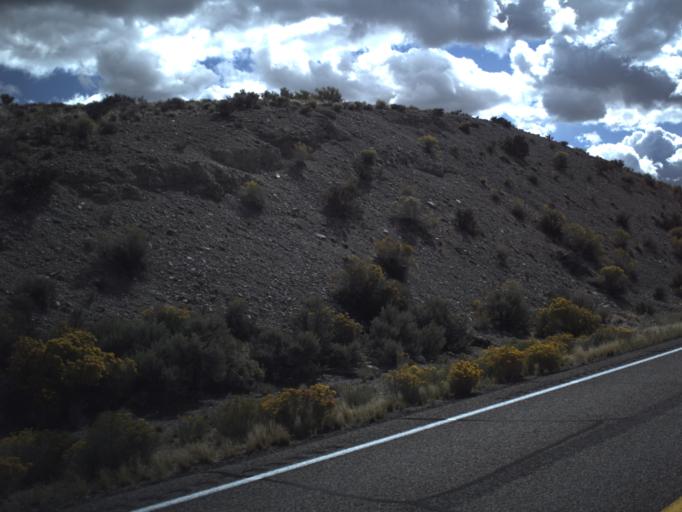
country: US
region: Nevada
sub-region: White Pine County
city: McGill
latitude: 38.8791
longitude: -114.0049
